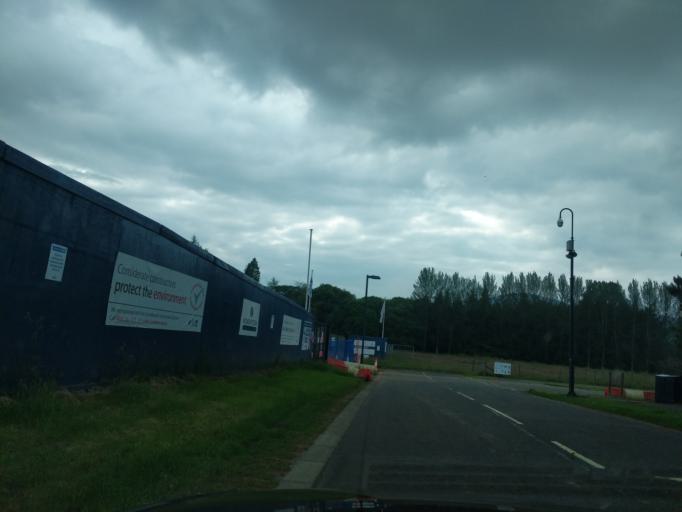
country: GB
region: Scotland
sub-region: Midlothian
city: Penicuik
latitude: 55.8567
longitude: -3.1994
